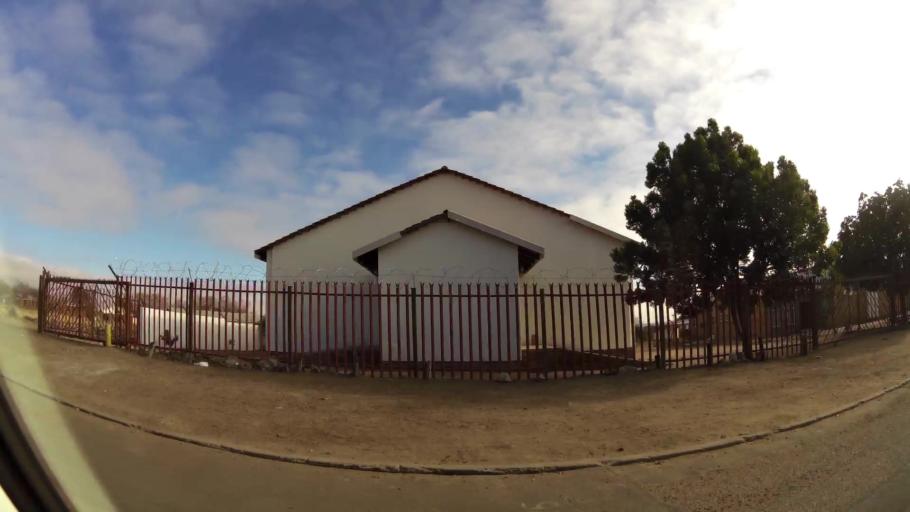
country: ZA
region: Limpopo
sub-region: Capricorn District Municipality
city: Polokwane
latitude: -23.8446
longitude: 29.3844
